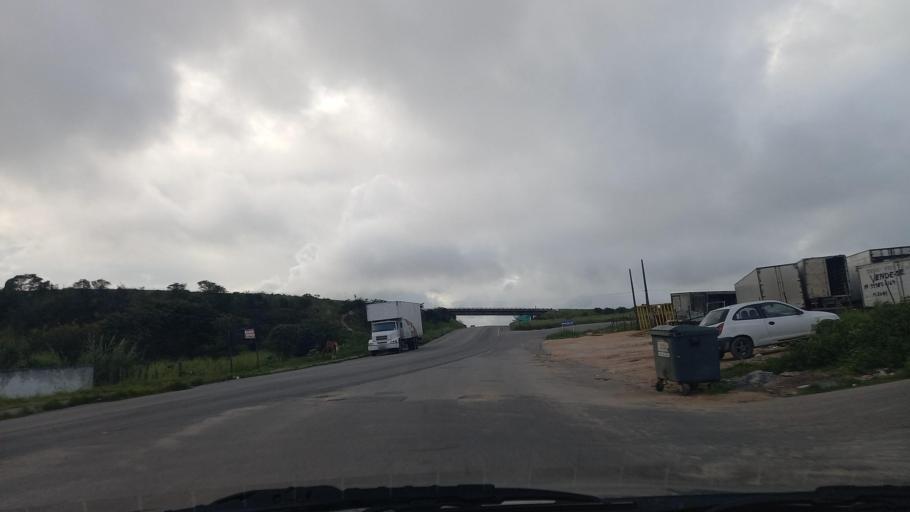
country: BR
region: Pernambuco
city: Garanhuns
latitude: -8.8796
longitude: -36.5069
